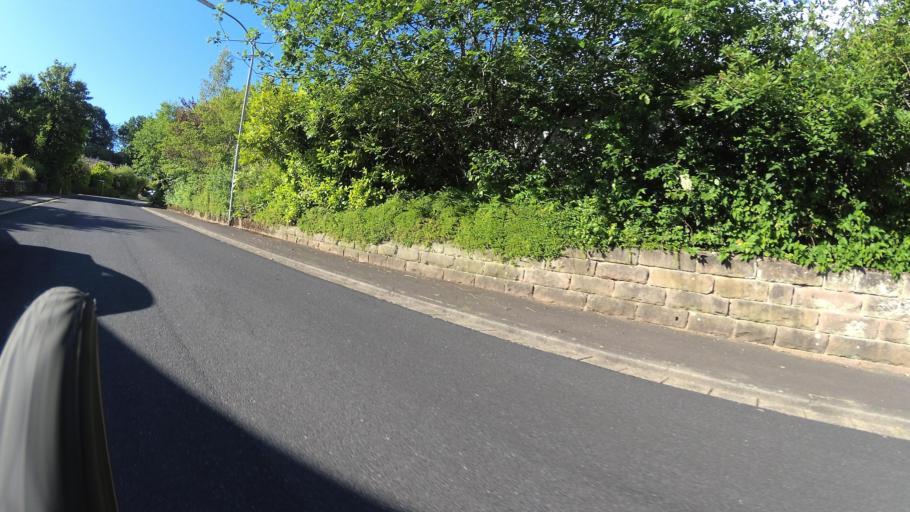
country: DE
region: Saarland
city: Merchweiler
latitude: 49.3566
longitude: 7.0054
